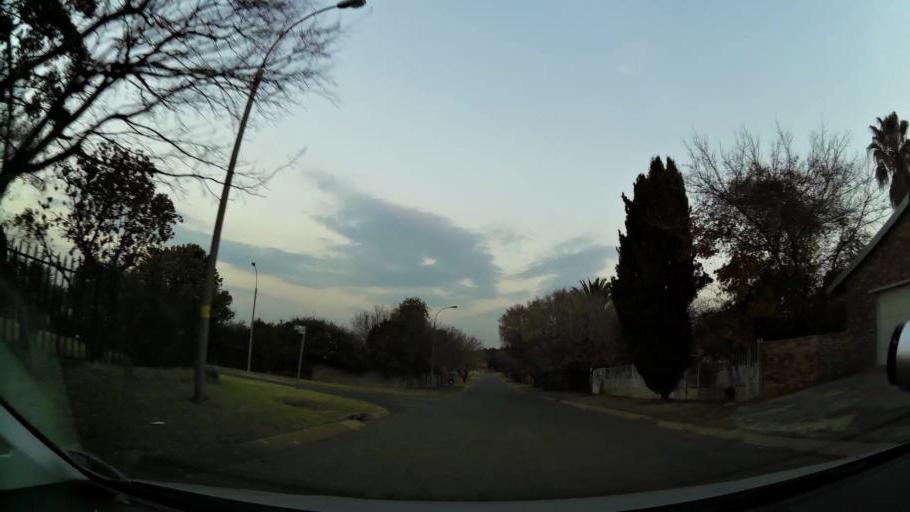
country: ZA
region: Gauteng
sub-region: Ekurhuleni Metropolitan Municipality
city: Tembisa
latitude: -26.0549
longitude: 28.2425
